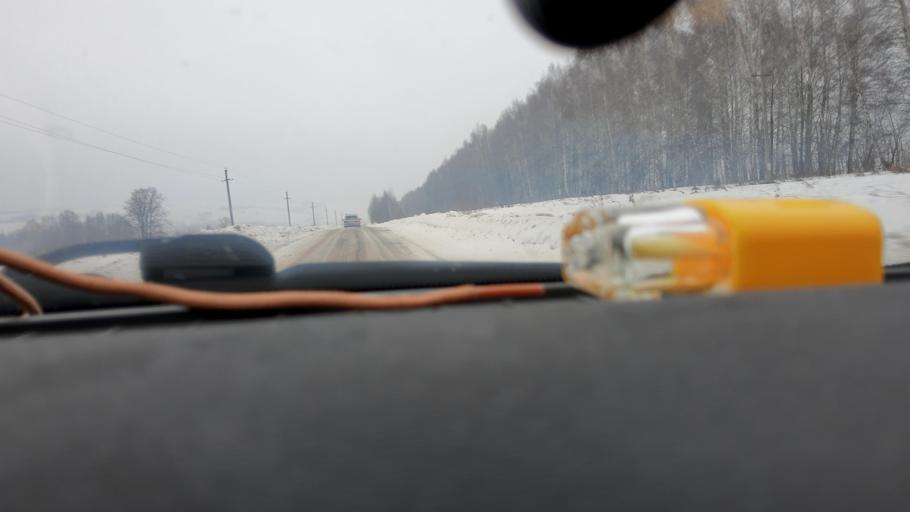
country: RU
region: Bashkortostan
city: Ulukulevo
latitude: 54.5654
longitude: 56.4320
